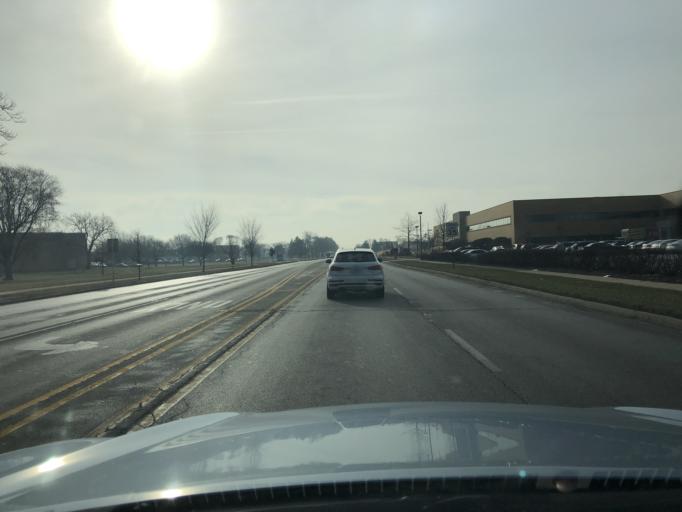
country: US
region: Illinois
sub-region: Cook County
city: Des Plaines
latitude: 42.0231
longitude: -87.9091
